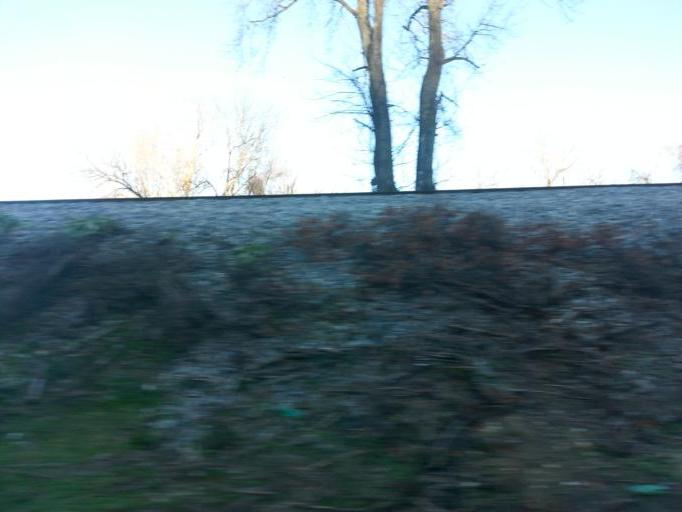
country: US
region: Tennessee
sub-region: Anderson County
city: Rocky Top
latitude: 36.2088
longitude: -84.1499
